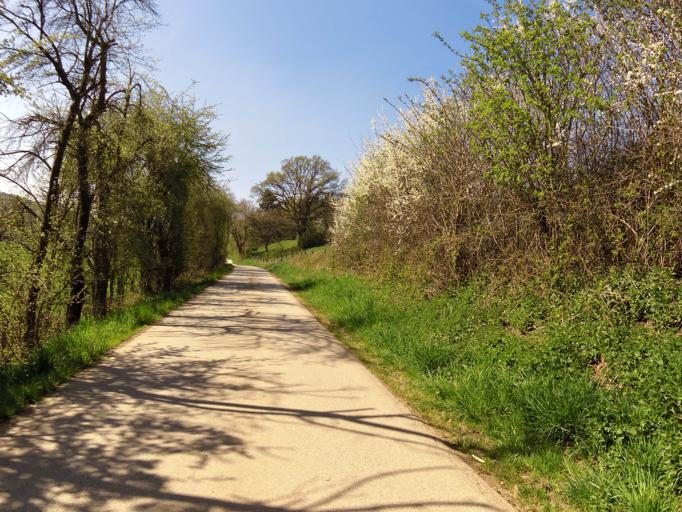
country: DE
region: North Rhine-Westphalia
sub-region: Regierungsbezirk Koln
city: Euskirchen
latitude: 50.6019
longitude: 6.8506
